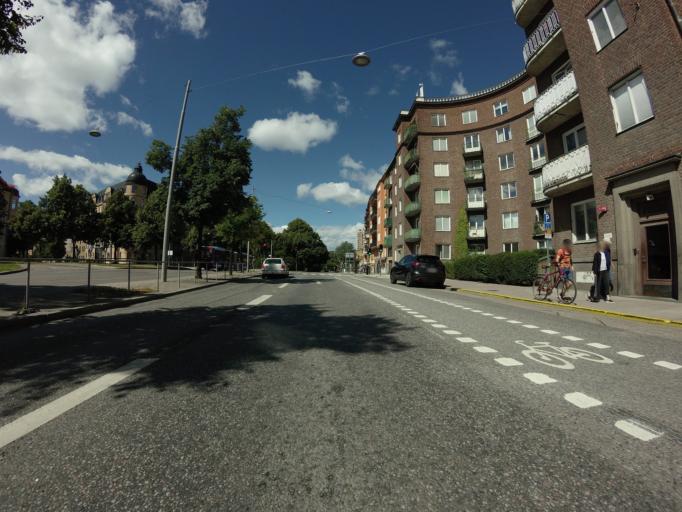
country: SE
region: Stockholm
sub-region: Stockholms Kommun
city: Stockholm
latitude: 59.3469
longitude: 18.0679
